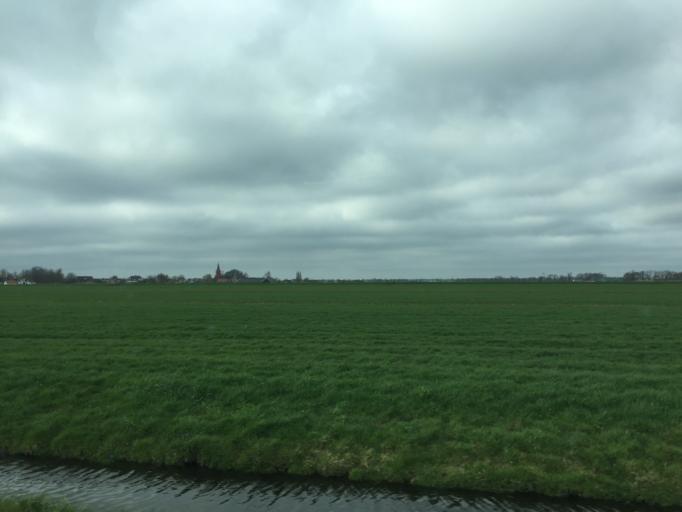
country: NL
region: South Holland
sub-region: Gemeente Leiderdorp
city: Leiderdorp
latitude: 52.1848
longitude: 4.5762
